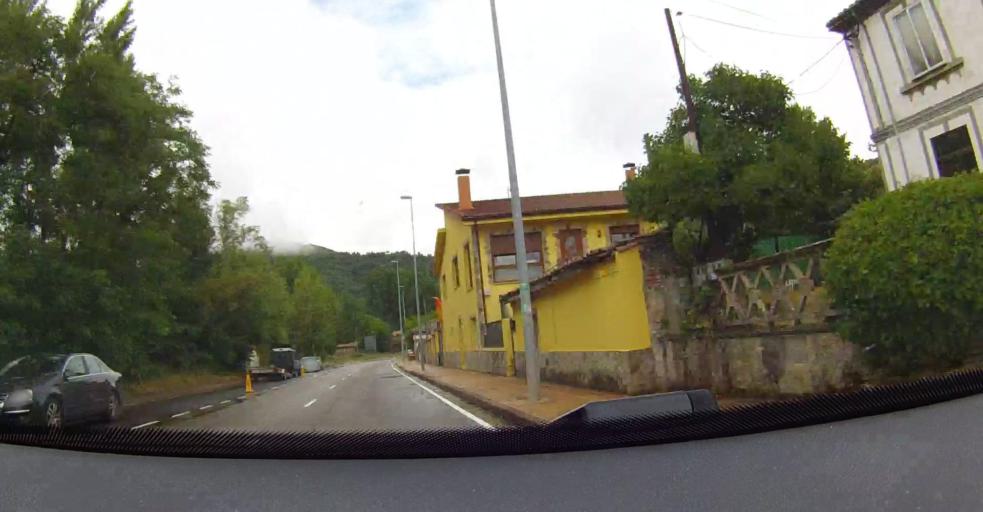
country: ES
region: Castille and Leon
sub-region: Provincia de Leon
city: Bonar
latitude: 42.8758
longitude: -5.3202
